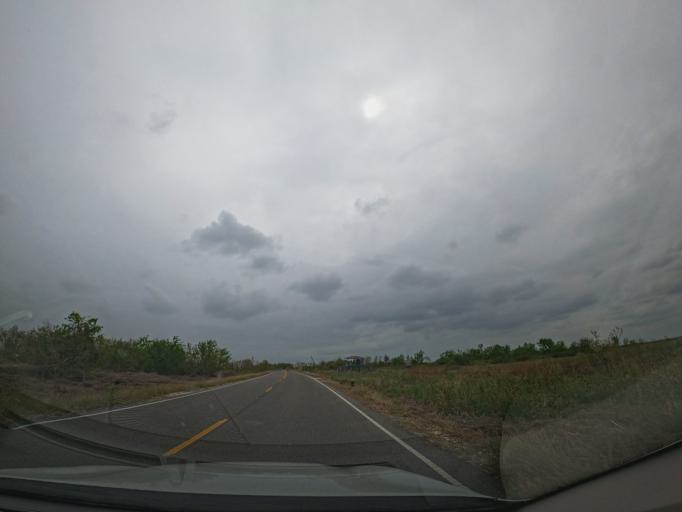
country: US
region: Louisiana
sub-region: Cameron Parish
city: Cameron
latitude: 29.7803
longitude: -93.3488
